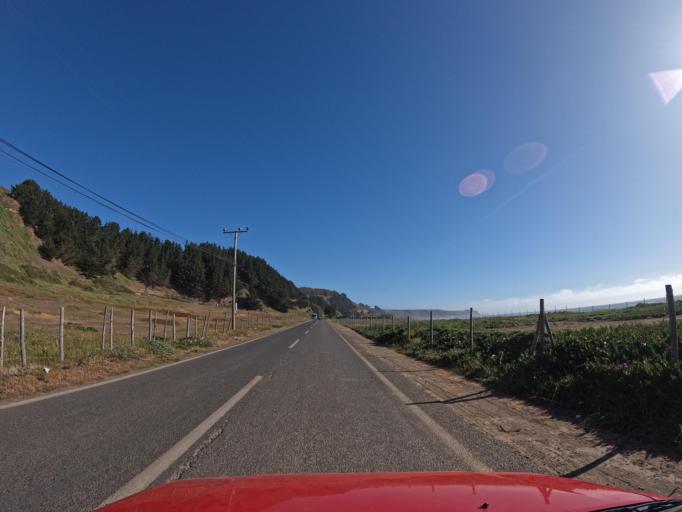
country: CL
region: Maule
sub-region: Provincia de Talca
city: Constitucion
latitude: -34.8646
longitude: -72.1480
